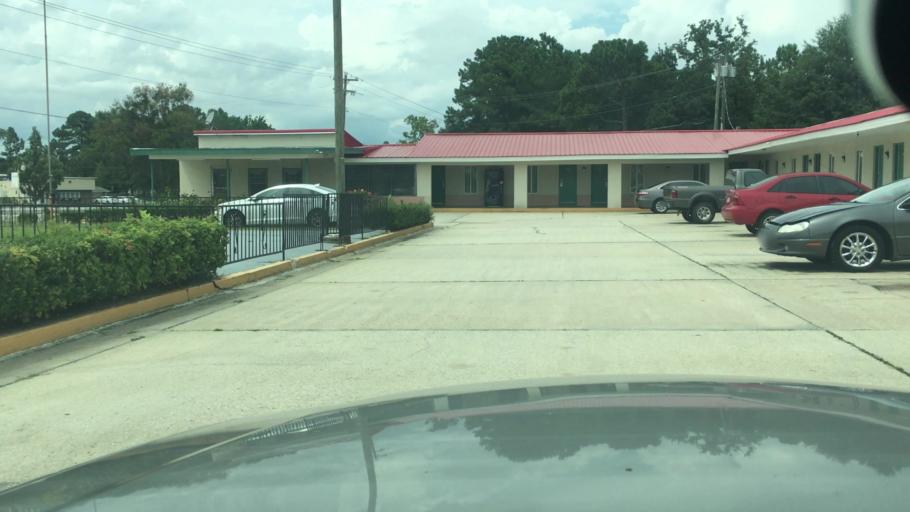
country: US
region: North Carolina
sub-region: Cumberland County
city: Fayetteville
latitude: 35.0058
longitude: -78.8982
